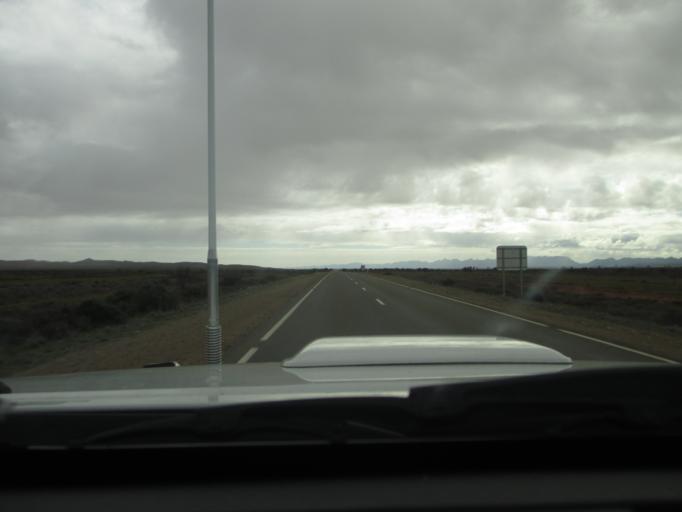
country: AU
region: South Australia
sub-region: Flinders Ranges
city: Quorn
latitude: -31.5413
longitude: 138.4247
